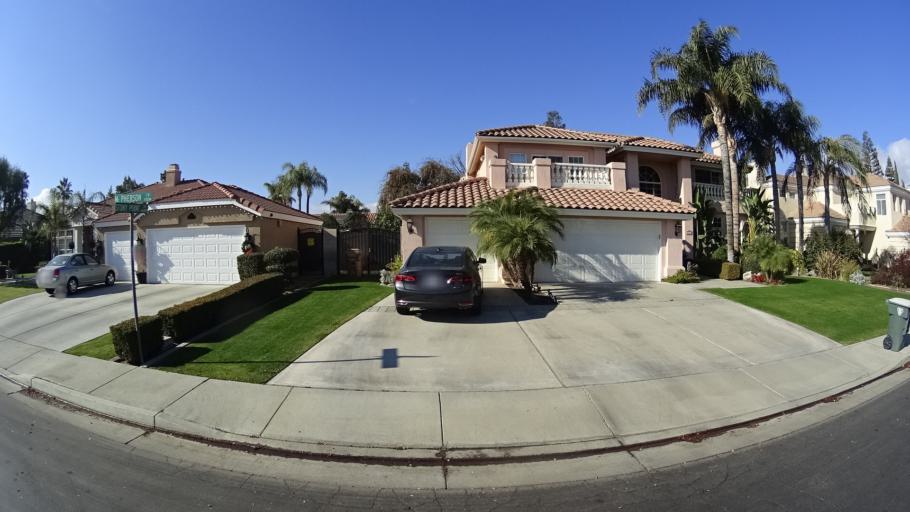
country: US
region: California
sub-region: Kern County
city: Greenacres
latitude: 35.3410
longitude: -119.1250
